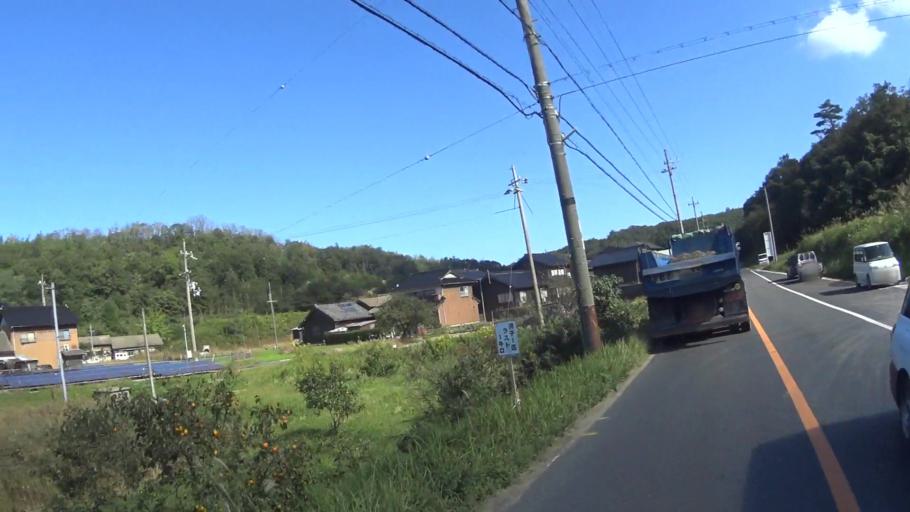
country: JP
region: Kyoto
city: Miyazu
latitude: 35.6986
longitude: 135.0595
